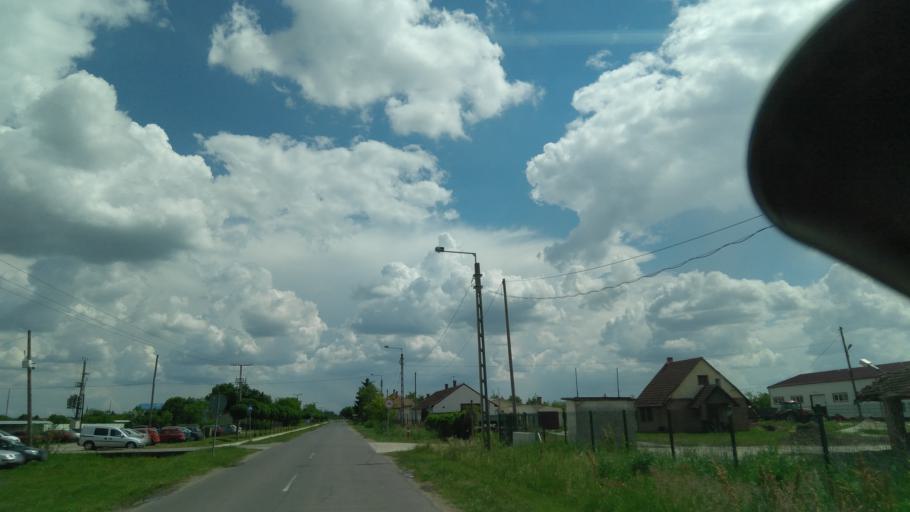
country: HU
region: Bekes
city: Devavanya
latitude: 47.0423
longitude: 20.9409
